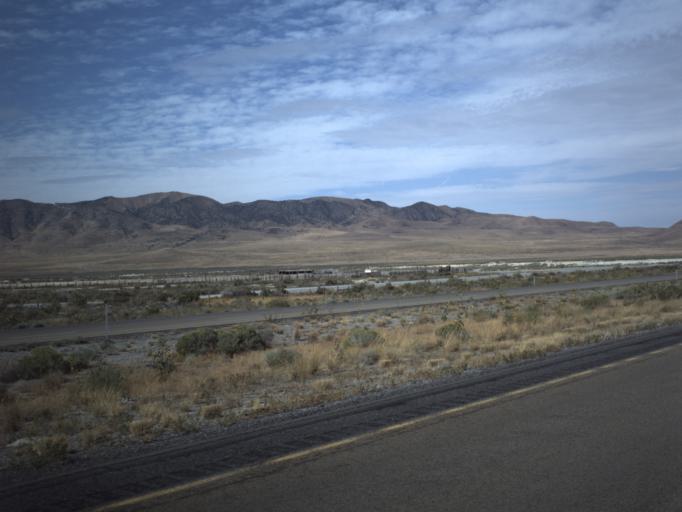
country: US
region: Utah
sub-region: Tooele County
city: Grantsville
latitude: 40.7709
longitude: -112.7958
